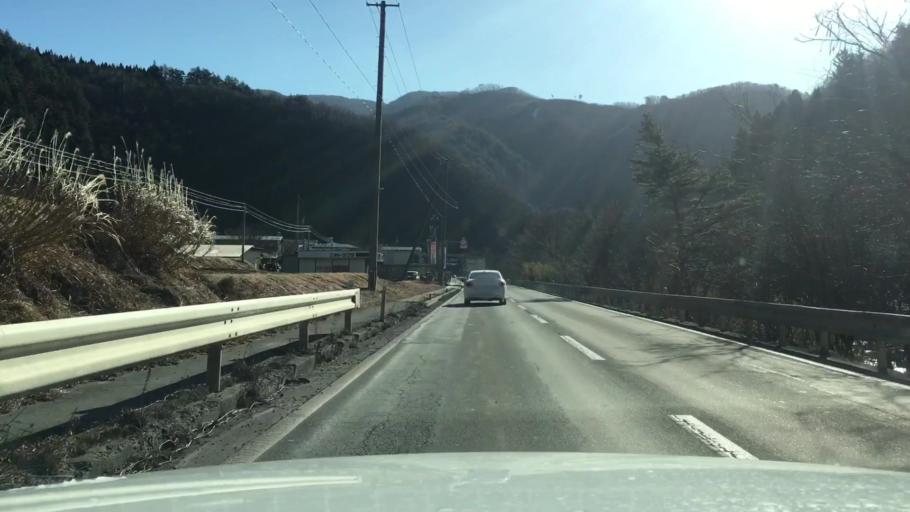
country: JP
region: Iwate
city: Miyako
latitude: 39.5948
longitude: 141.6608
